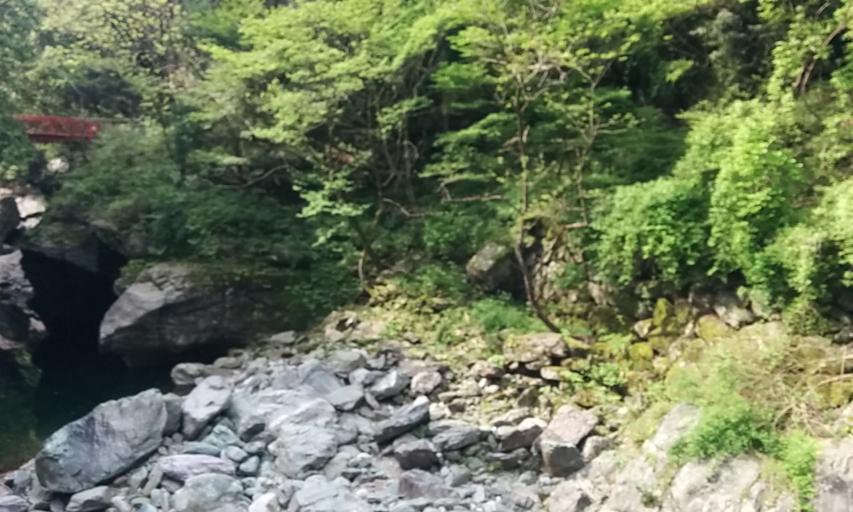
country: JP
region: Ehime
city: Niihama
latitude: 33.8984
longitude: 133.3079
